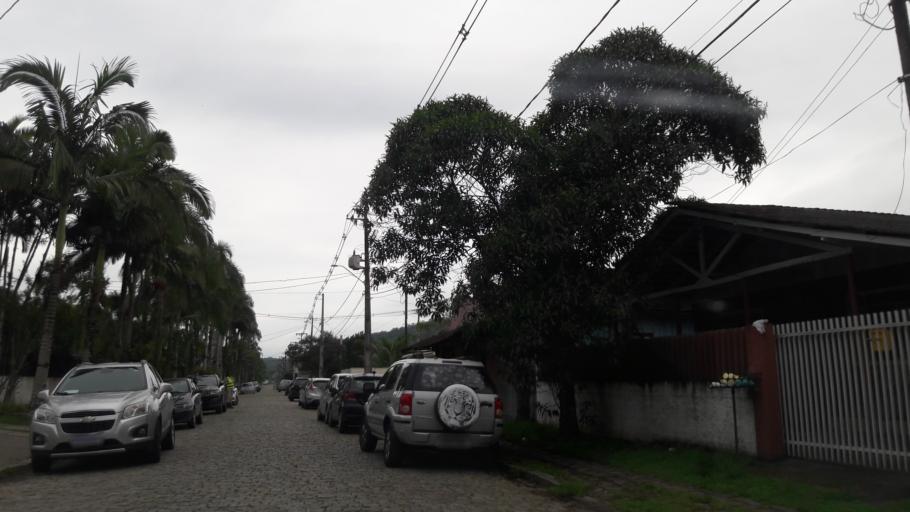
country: BR
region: Parana
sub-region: Antonina
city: Antonina
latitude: -25.4744
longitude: -48.8323
